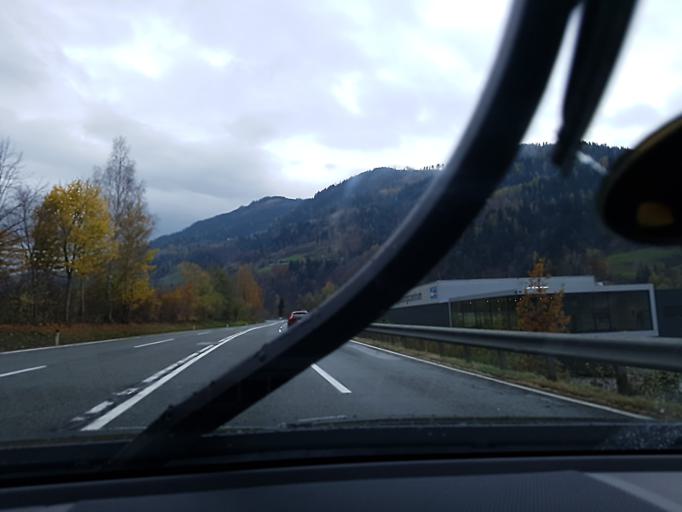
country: AT
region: Salzburg
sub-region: Politischer Bezirk Sankt Johann im Pongau
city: Bischofshofen
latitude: 47.3937
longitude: 13.2236
